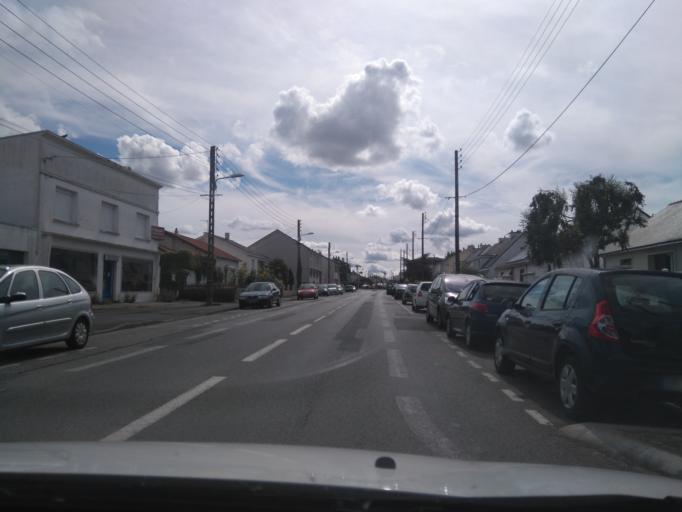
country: FR
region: Pays de la Loire
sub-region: Departement de la Loire-Atlantique
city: Reze
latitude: 47.1808
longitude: -1.5571
